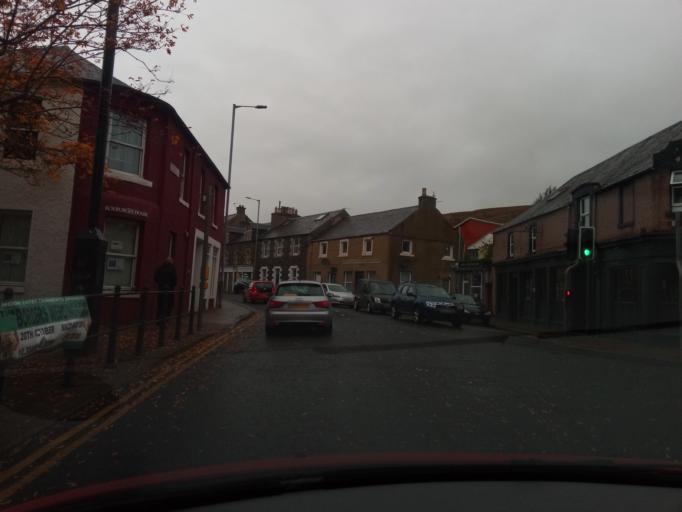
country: GB
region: Scotland
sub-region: The Scottish Borders
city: Galashiels
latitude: 55.6188
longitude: -2.8120
